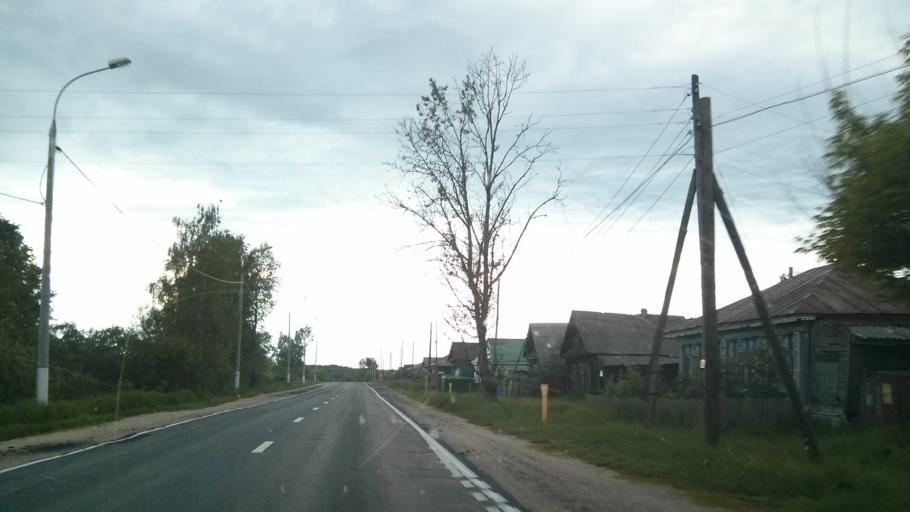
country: RU
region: Nizjnij Novgorod
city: Vacha
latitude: 55.7477
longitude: 42.4939
